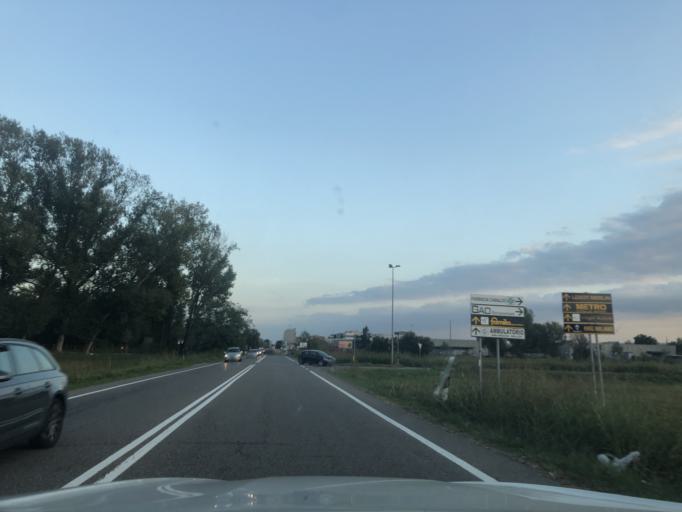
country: IT
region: Lombardy
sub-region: Citta metropolitana di Milano
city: Arese
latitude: 45.5480
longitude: 9.0943
